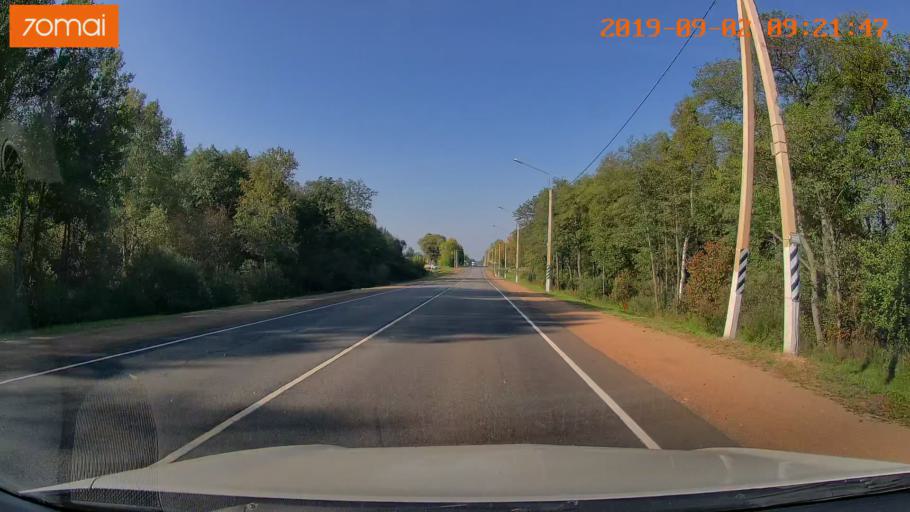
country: RU
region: Kaluga
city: Yukhnov
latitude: 54.7891
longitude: 35.3515
